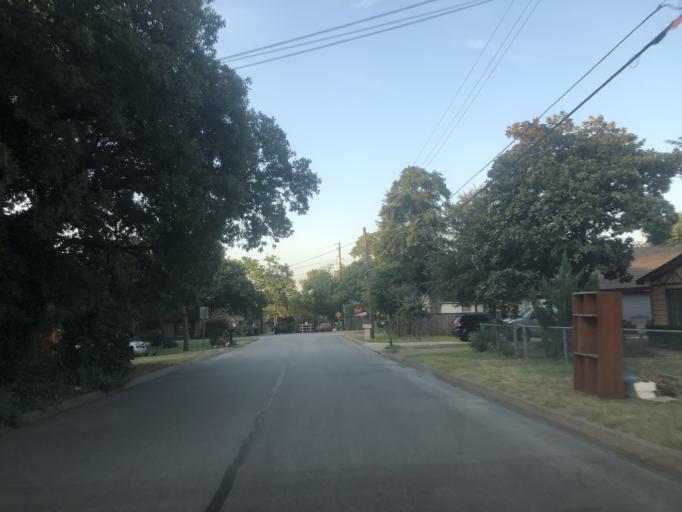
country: US
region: Texas
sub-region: Tarrant County
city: Lake Worth
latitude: 32.7999
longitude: -97.4497
